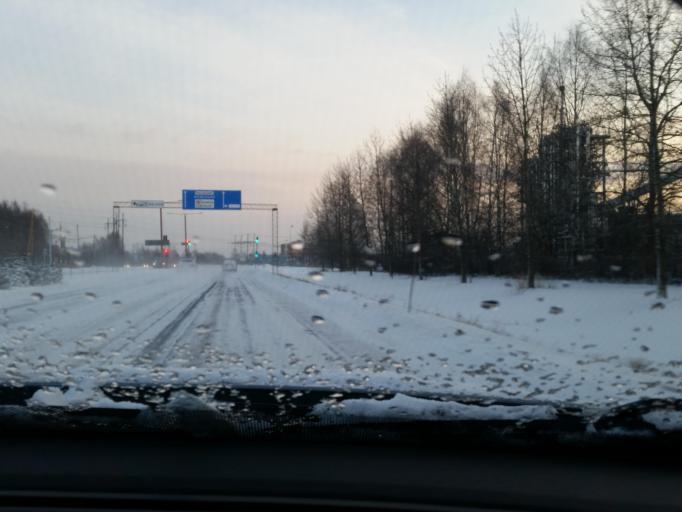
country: SE
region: Norrbotten
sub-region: Pitea Kommun
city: Pitea
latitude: 65.3167
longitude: 21.4531
